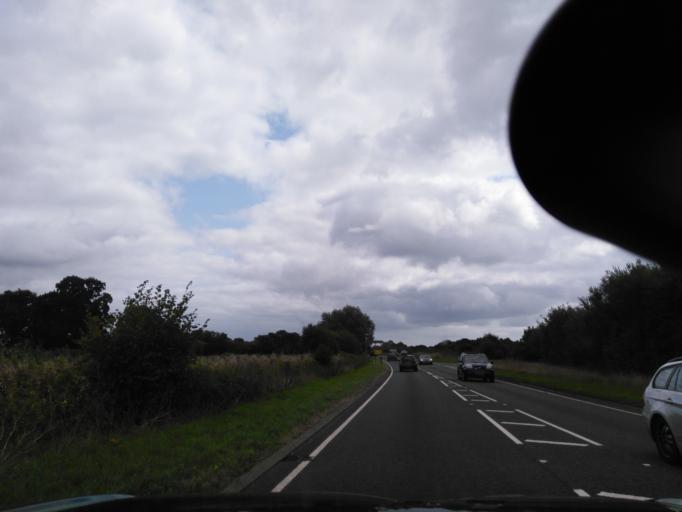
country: GB
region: England
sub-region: Dorset
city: Lytchett Matravers
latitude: 50.7338
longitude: -2.0736
